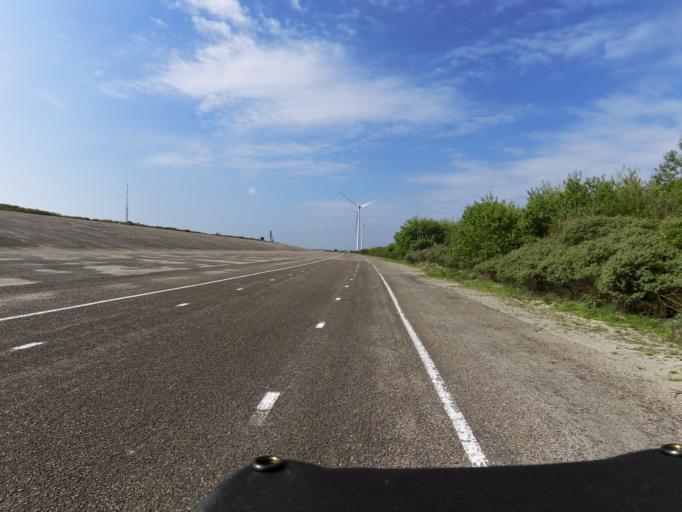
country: NL
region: Zeeland
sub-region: Gemeente Noord-Beveland
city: Kamperland
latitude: 51.6257
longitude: 3.6871
